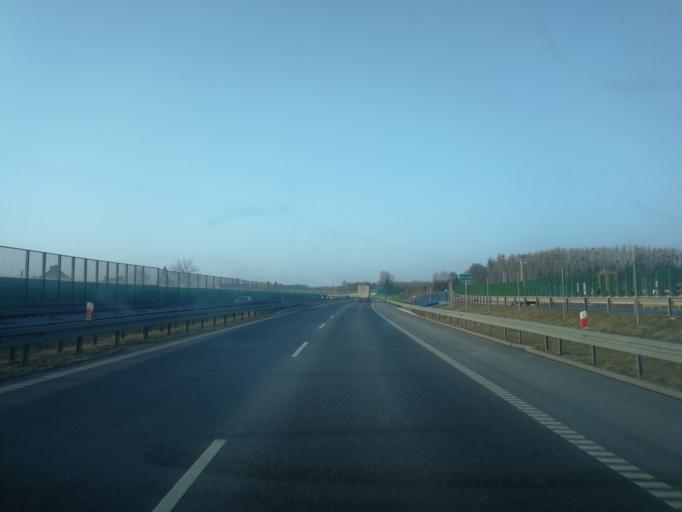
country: PL
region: Warmian-Masurian Voivodeship
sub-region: Powiat elblaski
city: Gronowo Gorne
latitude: 54.1268
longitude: 19.4609
